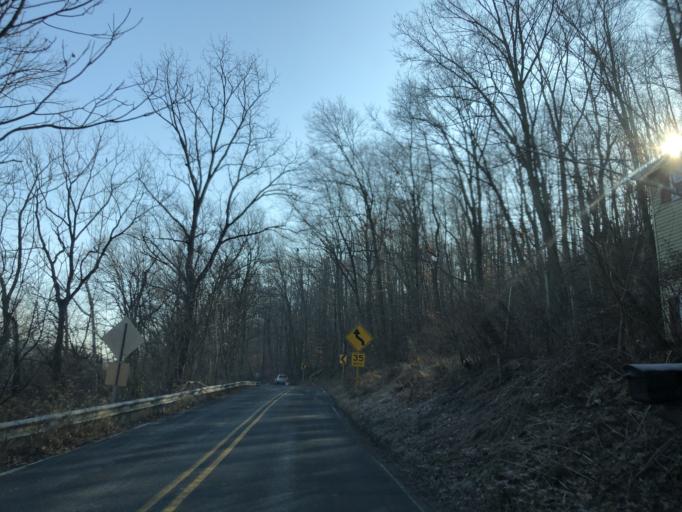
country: US
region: Pennsylvania
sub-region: Chester County
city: Downingtown
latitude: 39.9966
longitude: -75.7087
